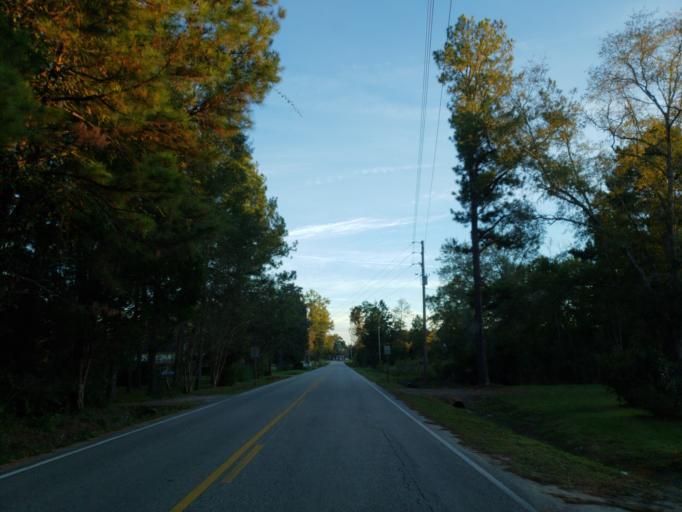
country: US
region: Mississippi
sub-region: Wayne County
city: Belmont
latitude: 31.4317
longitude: -88.4726
